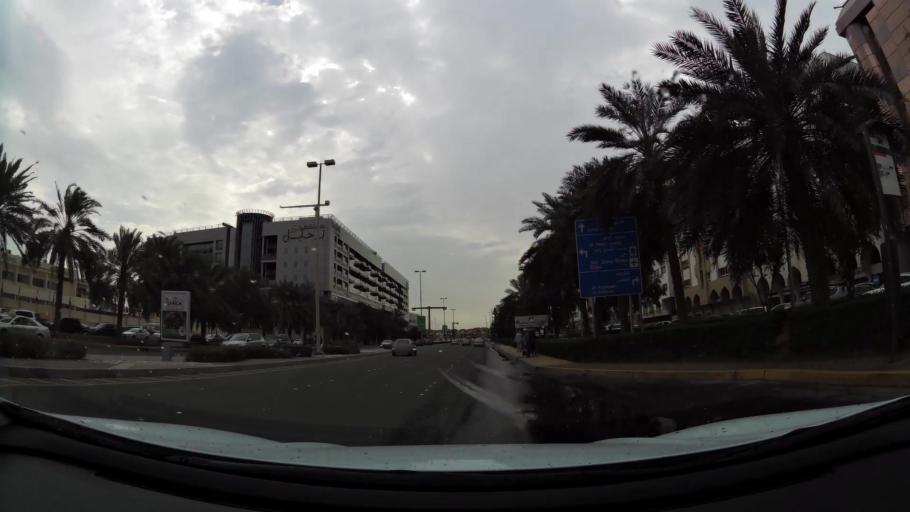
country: AE
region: Abu Dhabi
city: Abu Dhabi
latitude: 24.4799
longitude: 54.3794
